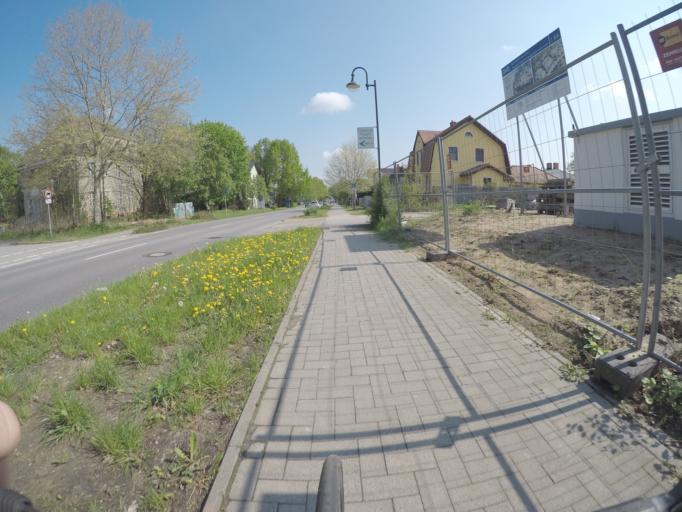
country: DE
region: Brandenburg
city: Wandlitz
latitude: 52.7455
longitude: 13.4621
